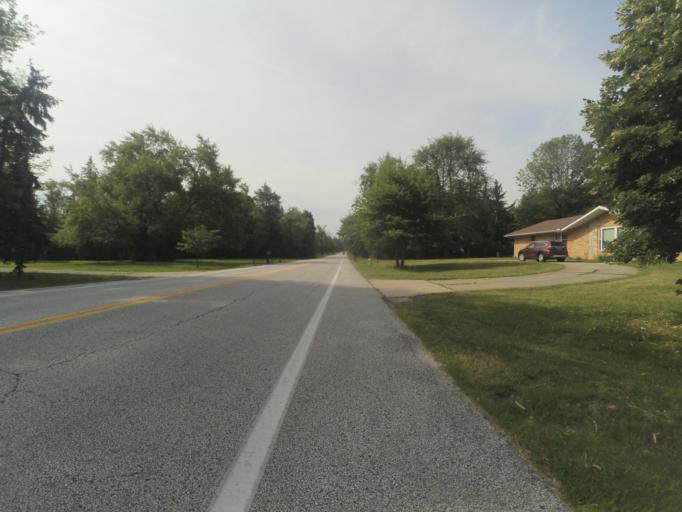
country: US
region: Ohio
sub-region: Cuyahoga County
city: Orange
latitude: 41.4585
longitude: -81.4802
